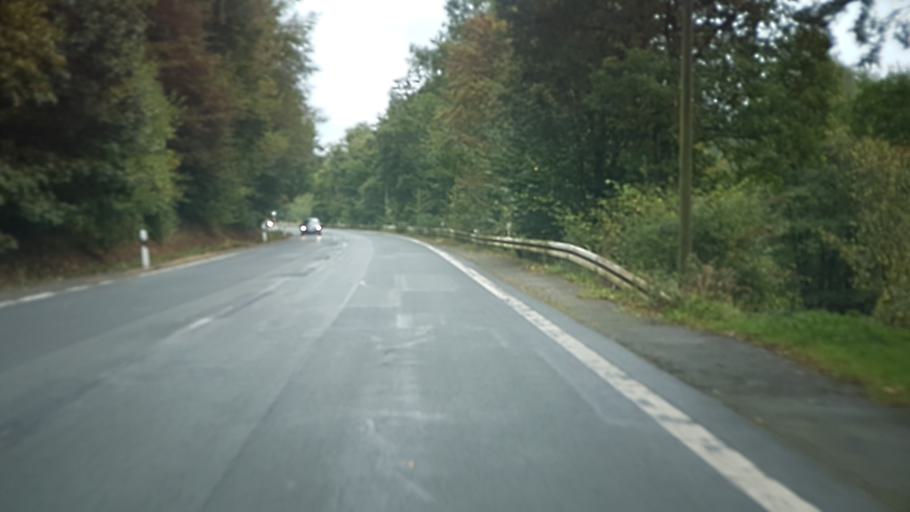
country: DE
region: North Rhine-Westphalia
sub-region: Regierungsbezirk Arnsberg
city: Herscheid
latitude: 51.1524
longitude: 7.7177
